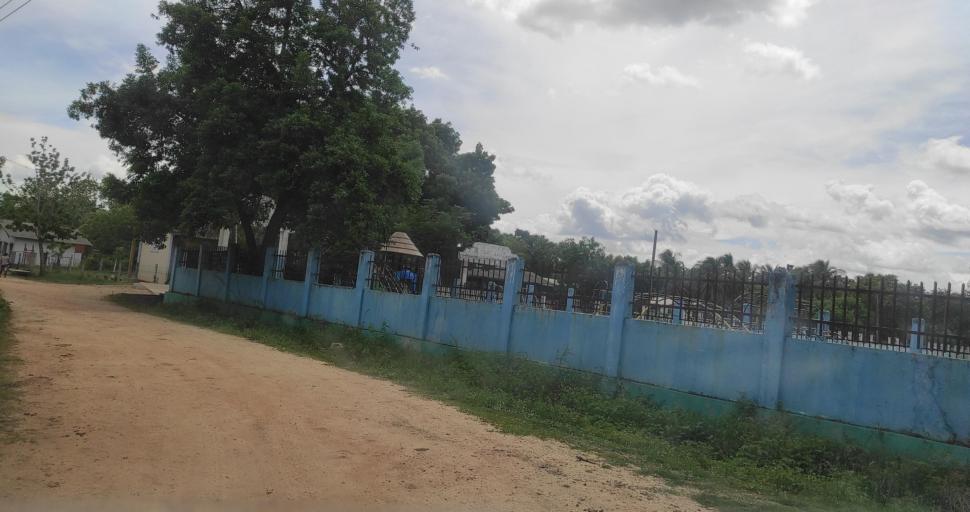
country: LK
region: Eastern Province
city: Trincomalee
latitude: 8.4409
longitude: 81.0490
